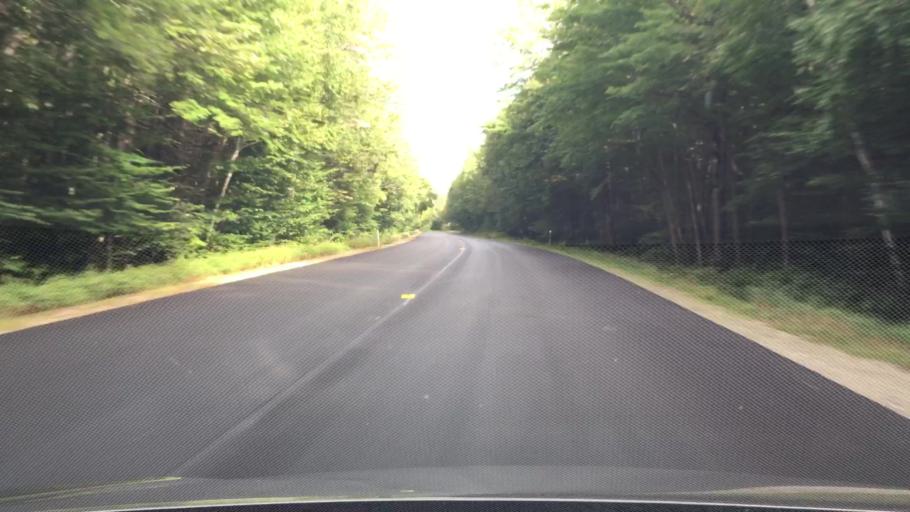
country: US
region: New Hampshire
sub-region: Carroll County
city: Tamworth
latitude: 44.0013
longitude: -71.4109
